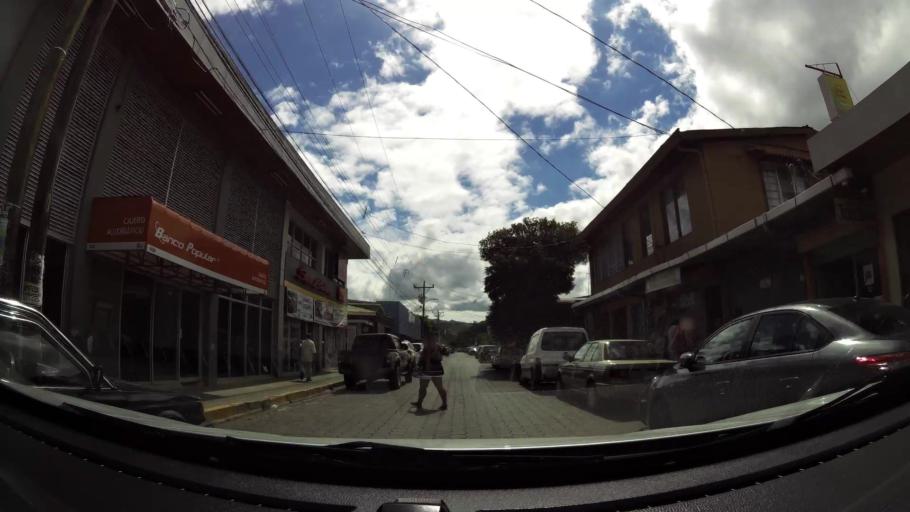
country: CR
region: Guanacaste
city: Santa Cruz
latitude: 10.2587
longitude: -85.5857
